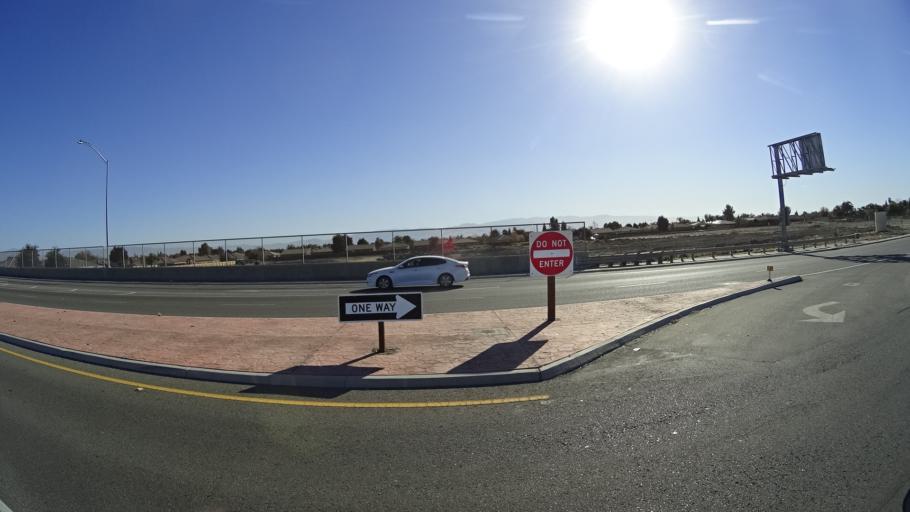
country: US
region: California
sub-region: Kern County
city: Greenfield
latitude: 35.2816
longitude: -119.0301
